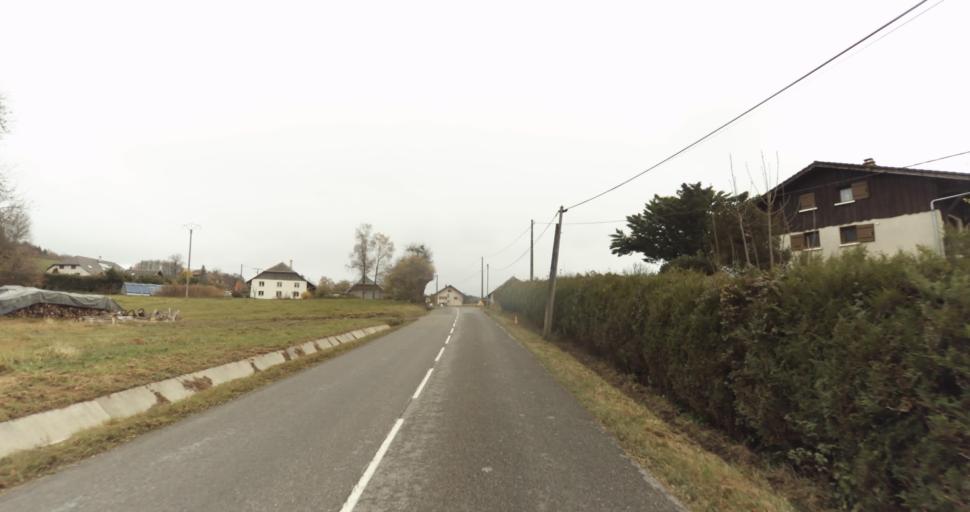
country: FR
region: Rhone-Alpes
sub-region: Departement de la Haute-Savoie
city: Evires
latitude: 46.0373
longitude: 6.2111
